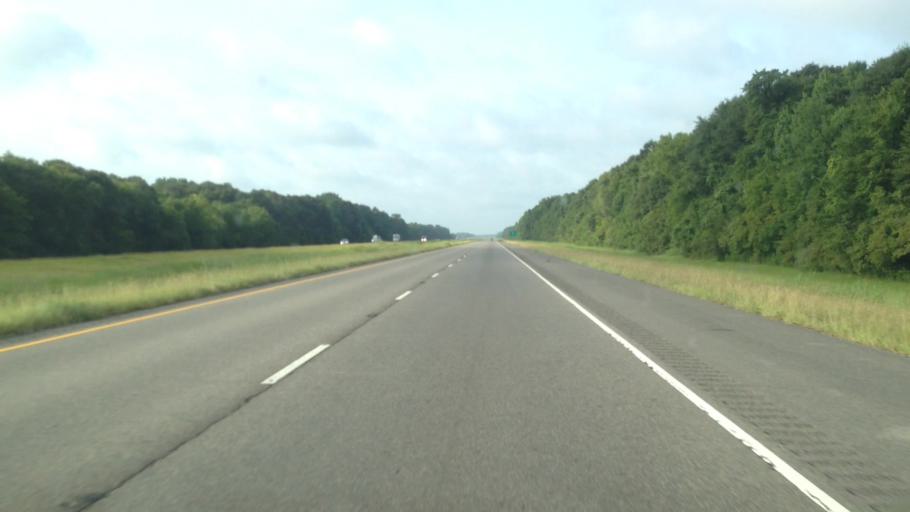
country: US
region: Louisiana
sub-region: Avoyelles Parish
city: Bunkie
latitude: 30.8915
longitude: -92.2272
